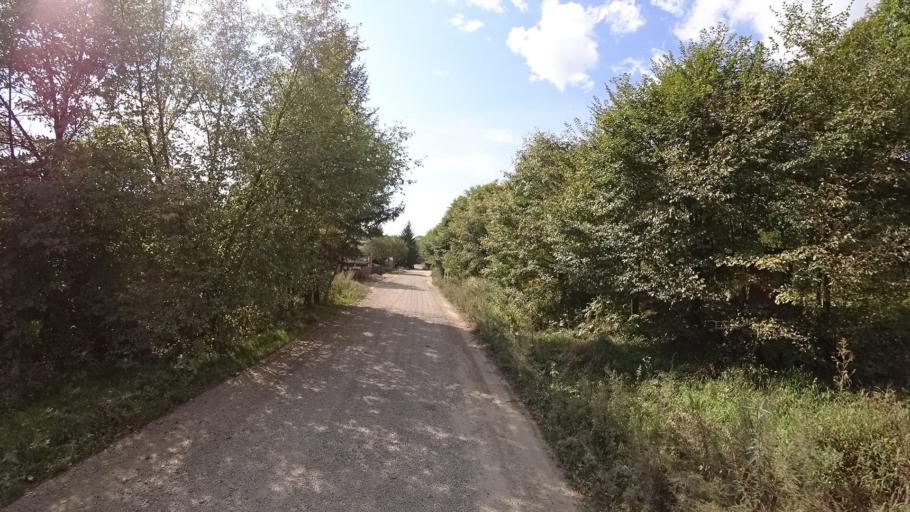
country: RU
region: Jewish Autonomous Oblast
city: Birakan
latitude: 49.0108
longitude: 131.7390
